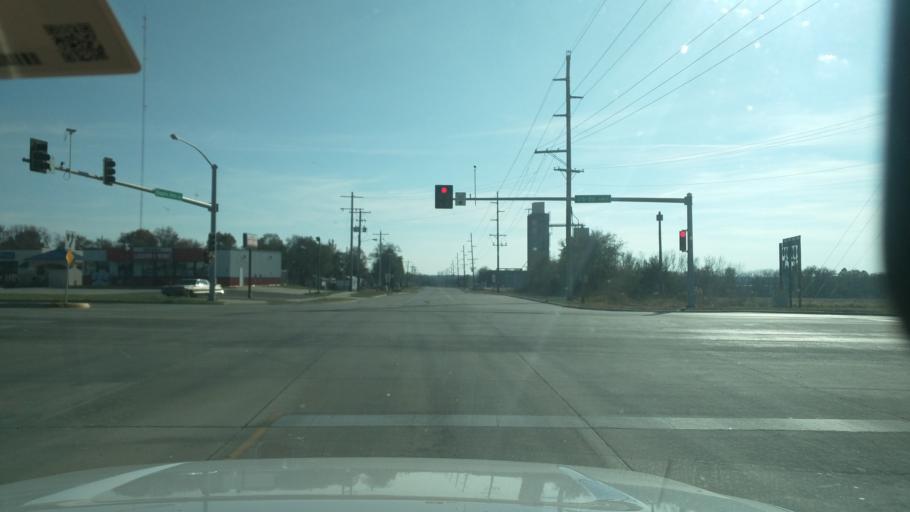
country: US
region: Kansas
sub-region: Lyon County
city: Emporia
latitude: 38.4121
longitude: -96.2263
